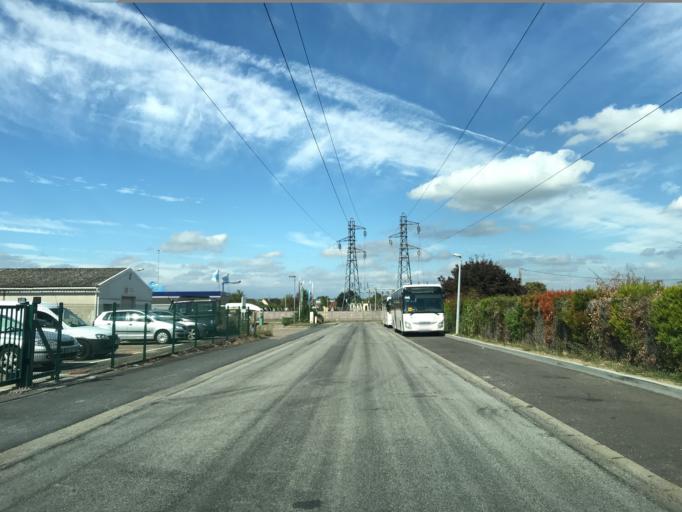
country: FR
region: Haute-Normandie
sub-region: Departement de l'Eure
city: Gaillon
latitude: 49.1683
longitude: 1.3503
